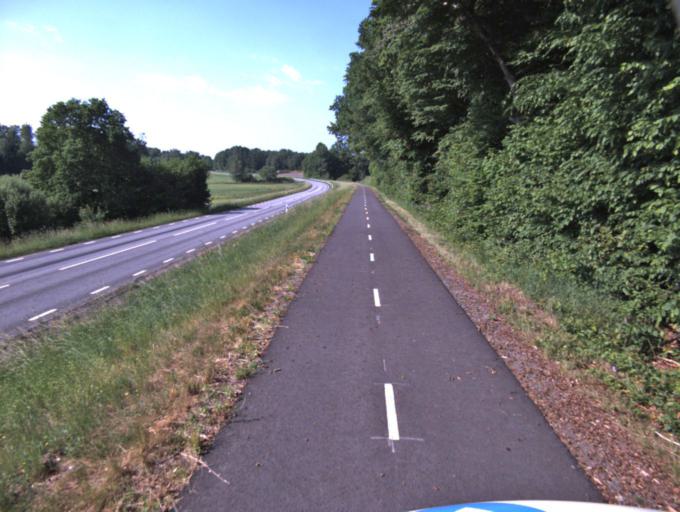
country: SE
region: Skane
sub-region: Kristianstads Kommun
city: Tollarp
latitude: 56.1537
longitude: 14.2652
